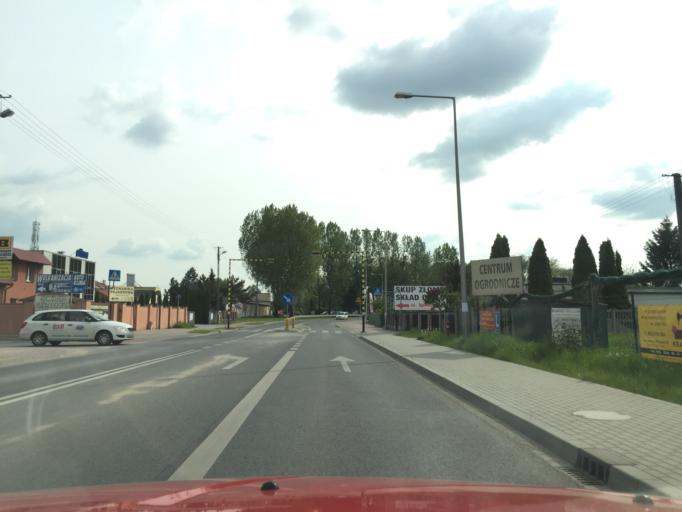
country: PL
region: Greater Poland Voivodeship
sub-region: Powiat poznanski
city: Plewiska
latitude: 52.3888
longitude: 16.7874
